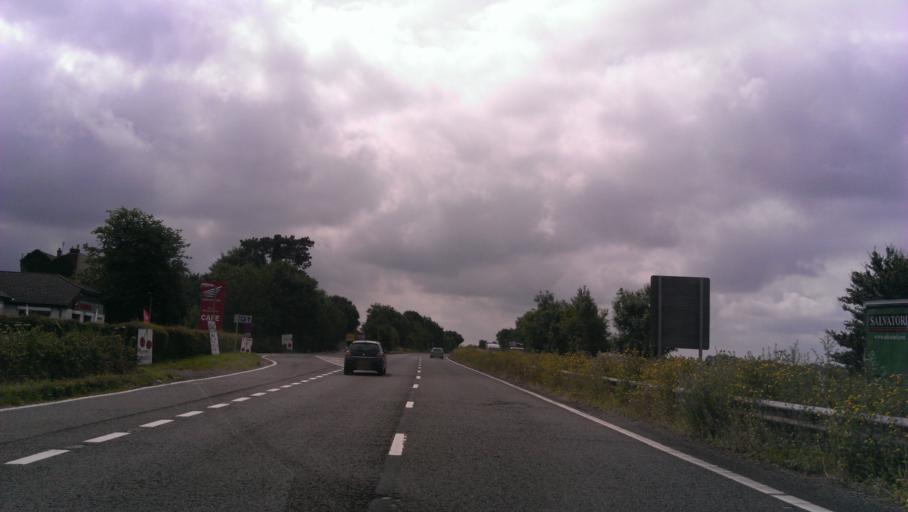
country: GB
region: England
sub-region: Kent
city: Wootton
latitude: 51.1942
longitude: 1.1850
